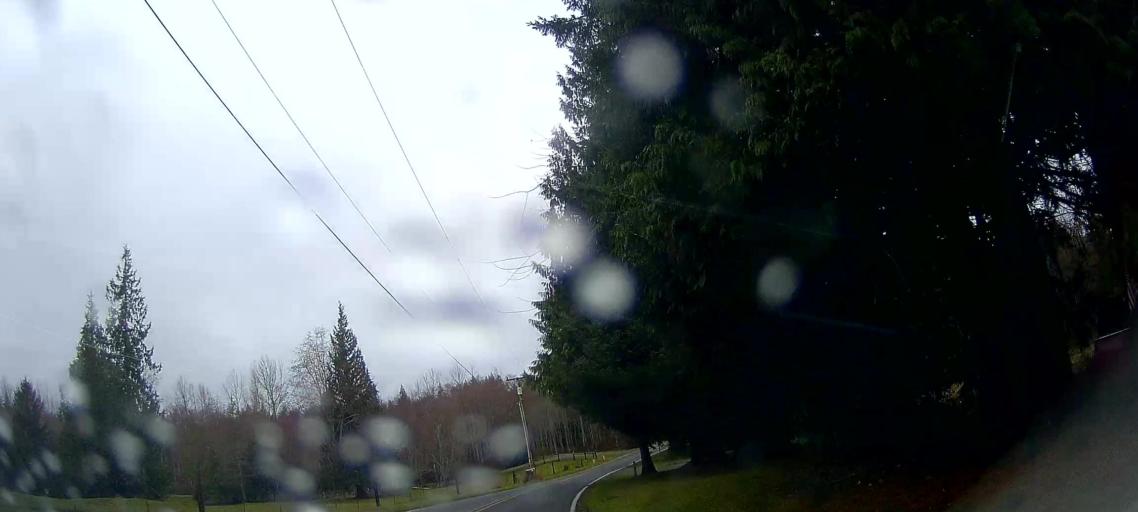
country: US
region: Washington
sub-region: Skagit County
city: Clear Lake
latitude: 48.4755
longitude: -122.1661
